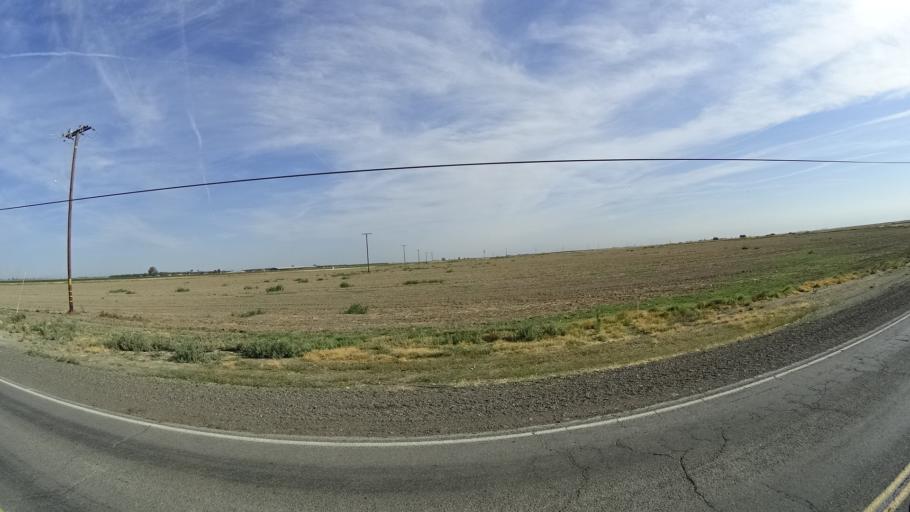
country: US
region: California
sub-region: Kings County
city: Home Garden
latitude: 36.3429
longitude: -119.5379
